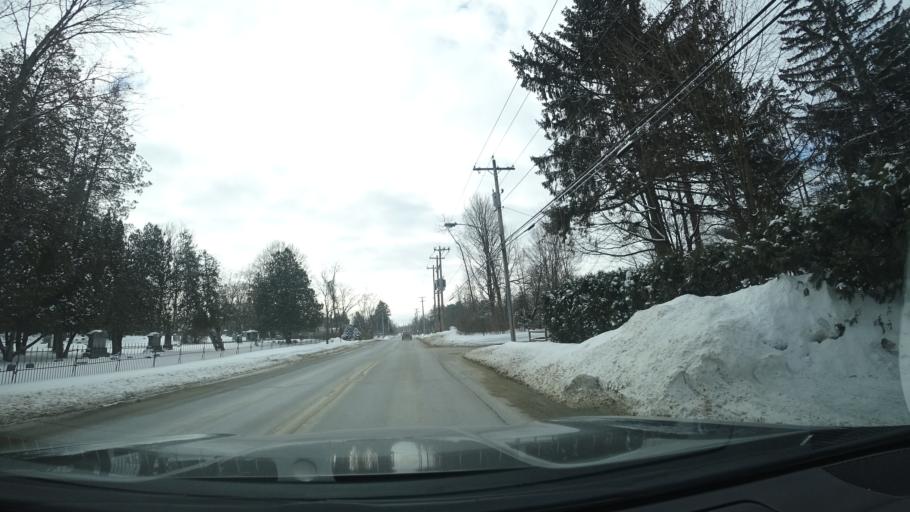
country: US
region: New York
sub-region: Saratoga County
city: South Glens Falls
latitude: 43.2908
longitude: -73.6276
